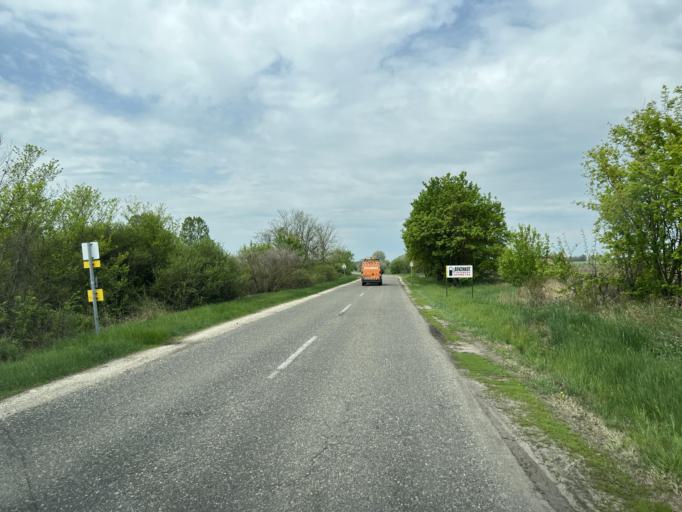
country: HU
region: Pest
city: Tortel
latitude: 47.1323
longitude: 19.9117
